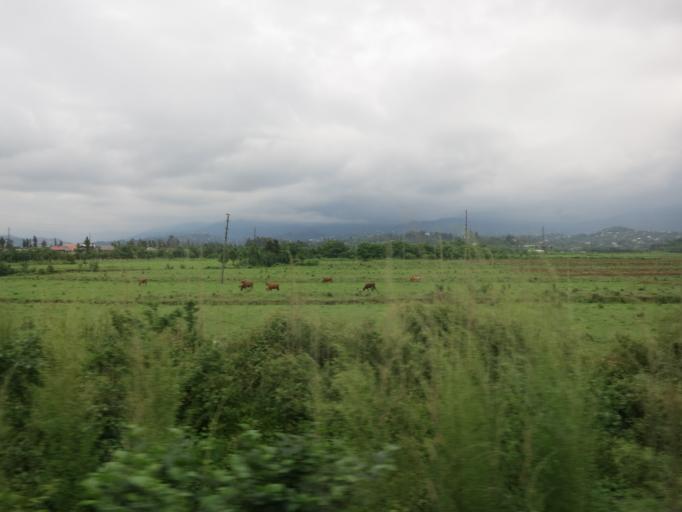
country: GE
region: Ajaria
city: Kobuleti
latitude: 41.7982
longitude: 41.7732
